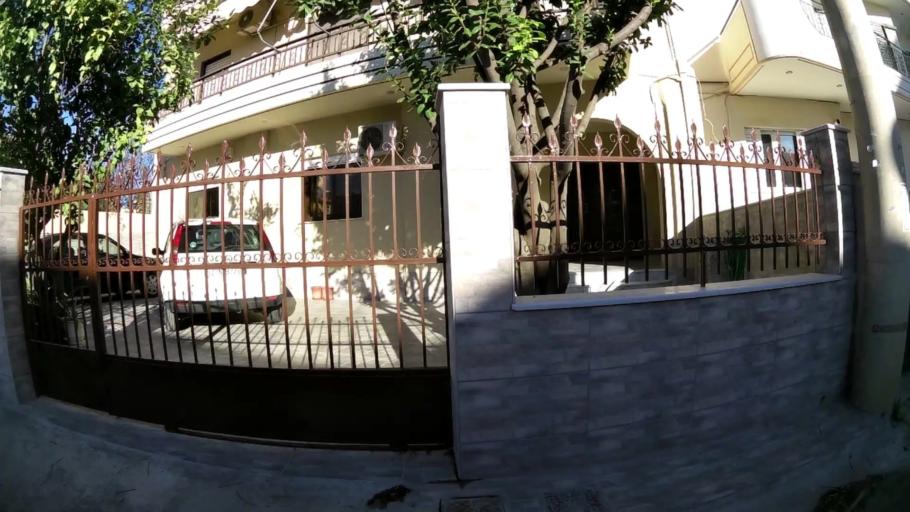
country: GR
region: Attica
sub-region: Nomarchia Anatolikis Attikis
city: Acharnes
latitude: 38.0898
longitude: 23.7339
